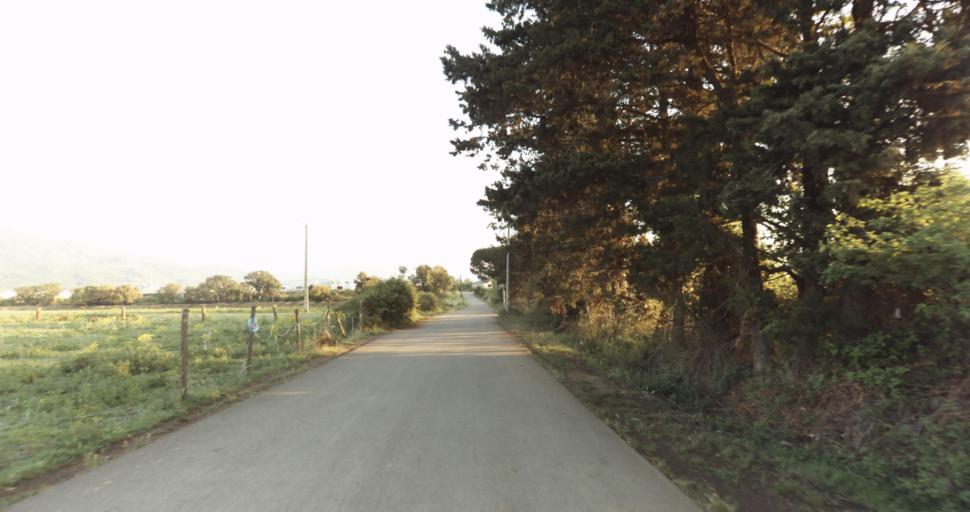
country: FR
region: Corsica
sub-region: Departement de la Haute-Corse
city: Biguglia
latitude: 42.6020
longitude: 9.4537
